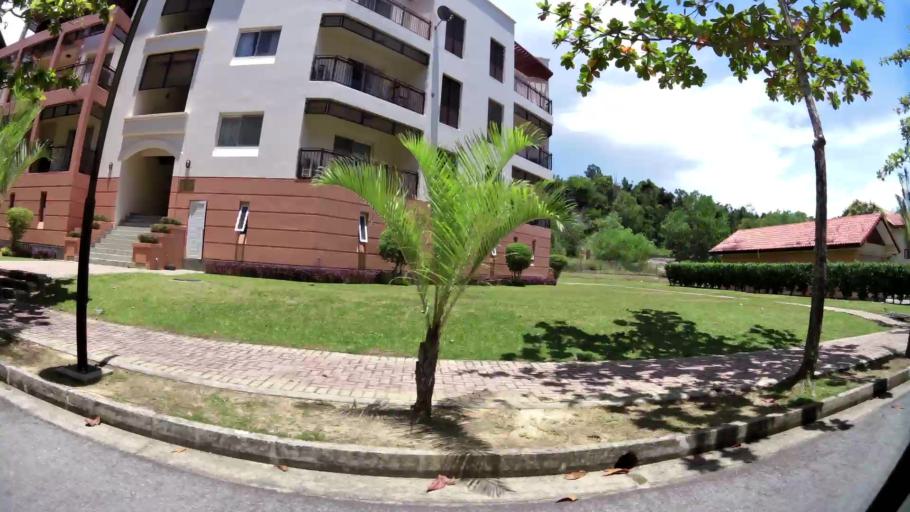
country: BN
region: Brunei and Muara
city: Bandar Seri Begawan
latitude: 4.9525
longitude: 114.8928
